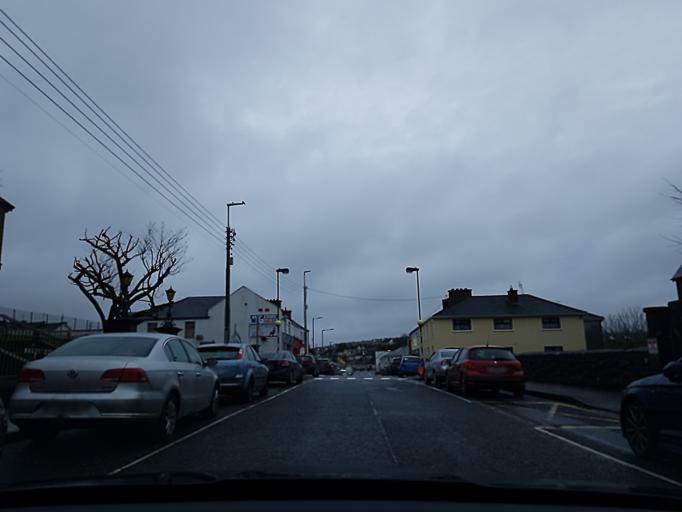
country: IE
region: Connaught
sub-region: Maigh Eo
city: Castlebar
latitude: 53.8584
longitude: -9.3007
